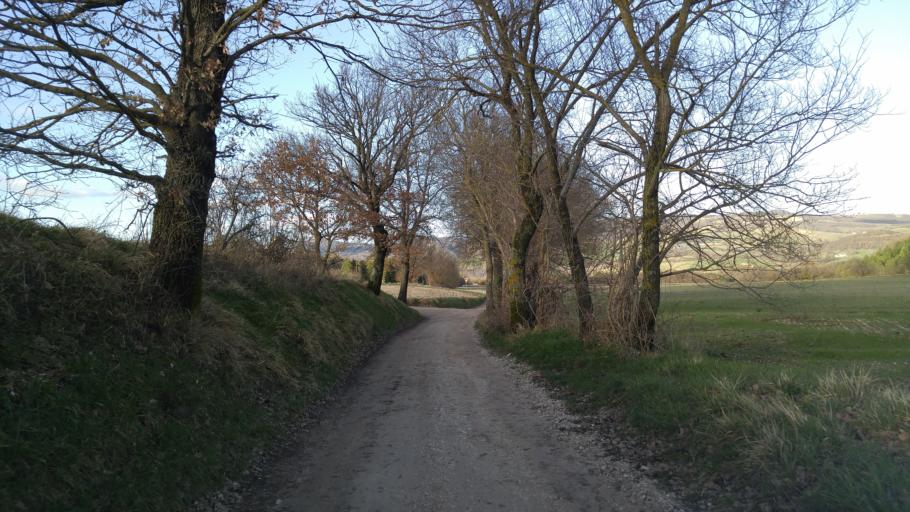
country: IT
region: The Marches
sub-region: Provincia di Pesaro e Urbino
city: Cagli
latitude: 43.5365
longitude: 12.6944
